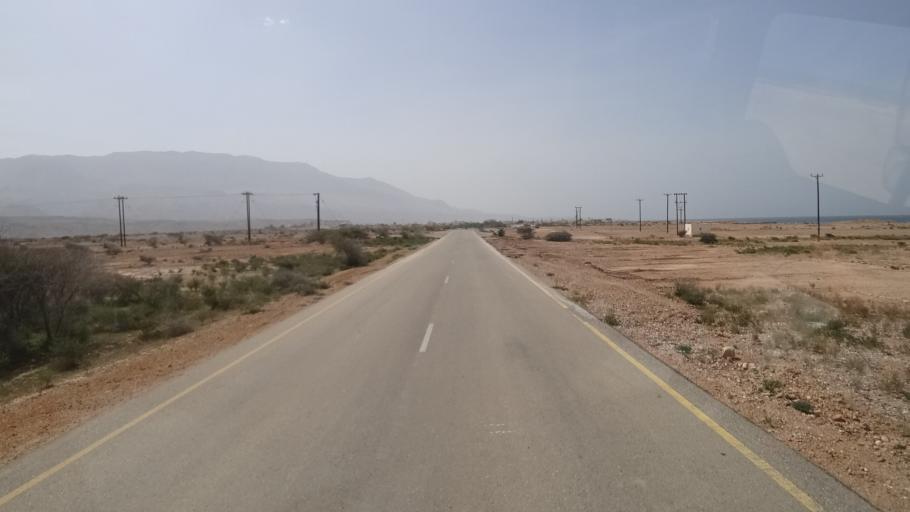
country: OM
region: Ash Sharqiyah
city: Sur
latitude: 22.9832
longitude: 59.1489
